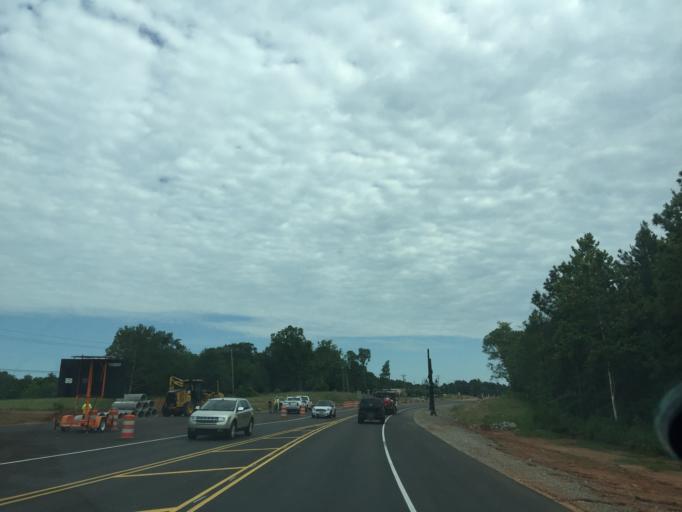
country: US
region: Mississippi
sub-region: Rankin County
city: Brandon
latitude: 32.2942
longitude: -89.9967
